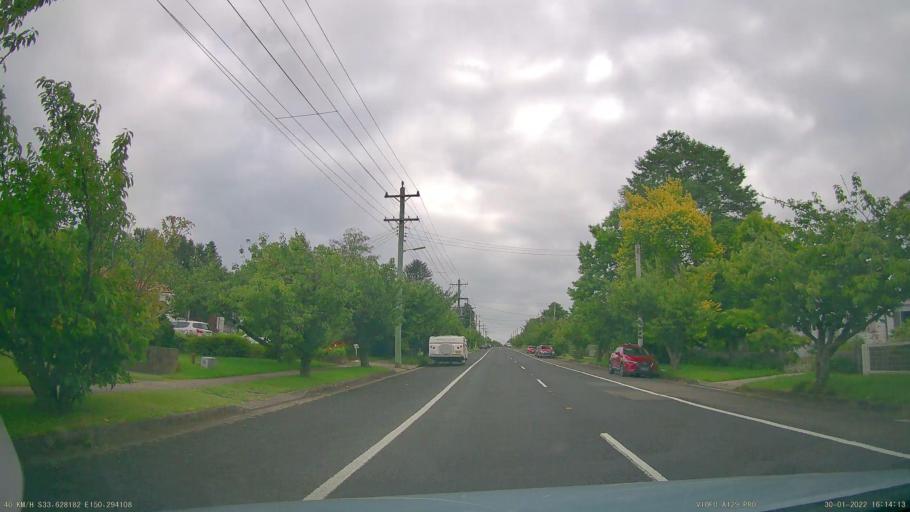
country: AU
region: New South Wales
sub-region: Blue Mountains Municipality
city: Blackheath
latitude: -33.6282
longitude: 150.2940
